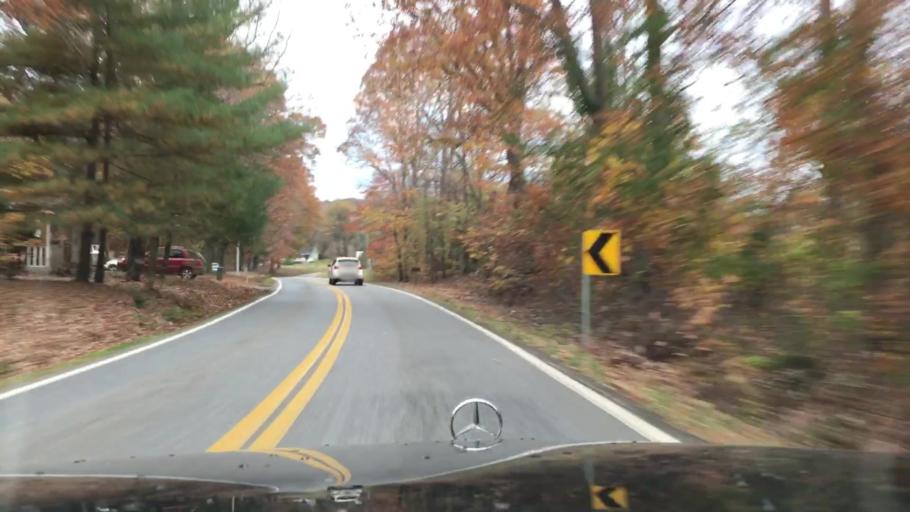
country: US
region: Virginia
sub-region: Campbell County
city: Timberlake
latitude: 37.2349
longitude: -79.2803
